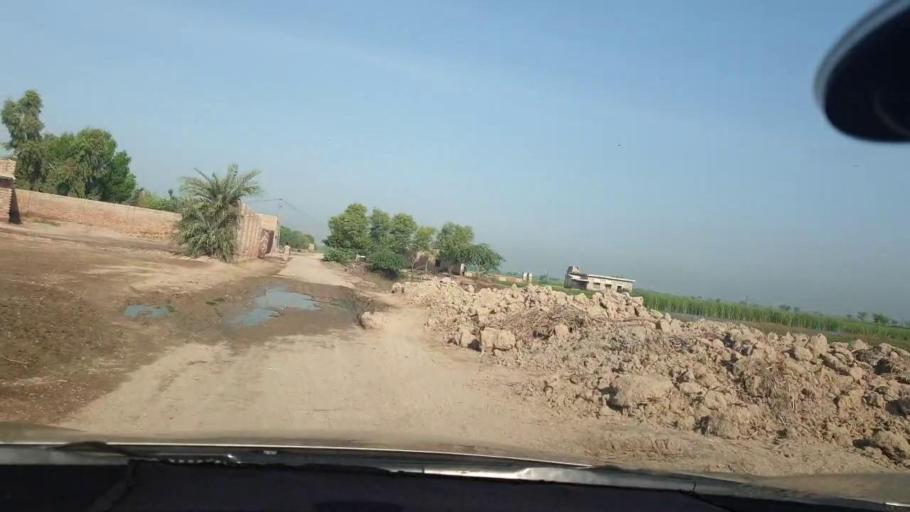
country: PK
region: Sindh
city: Kambar
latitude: 27.6547
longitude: 68.0319
